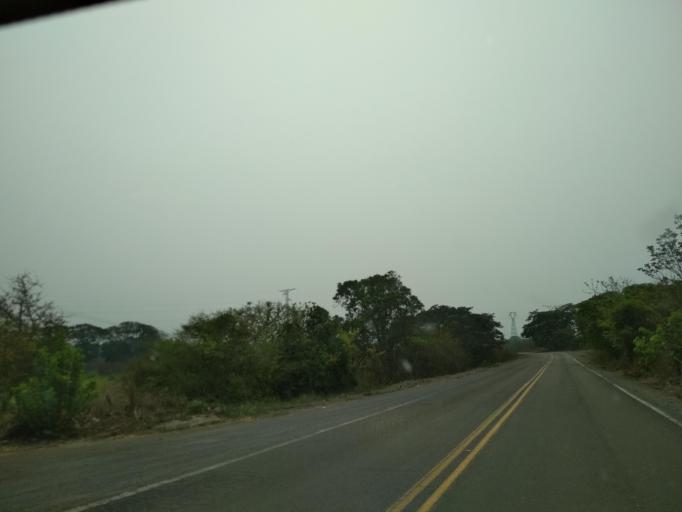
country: MX
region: Veracruz
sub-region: Veracruz
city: Delfino Victoria (Santa Fe)
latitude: 19.2033
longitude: -96.3132
